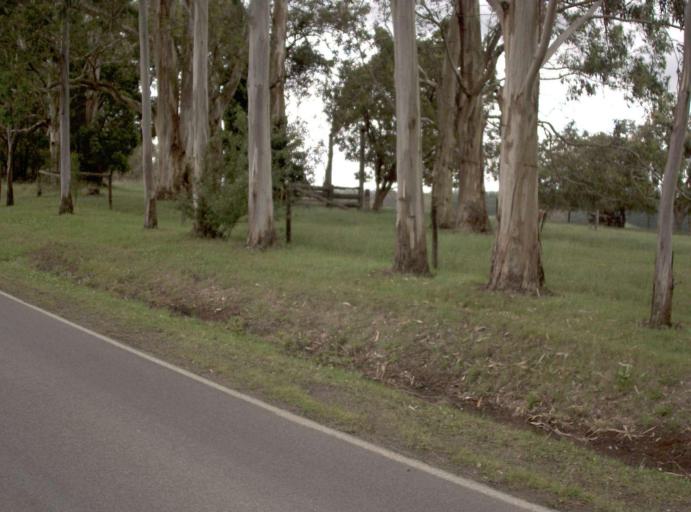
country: AU
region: Victoria
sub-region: Baw Baw
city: Warragul
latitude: -38.0636
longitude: 145.9666
